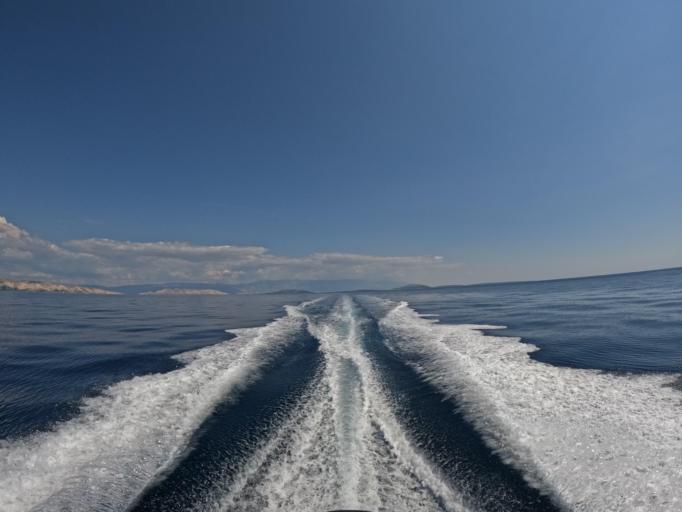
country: HR
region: Primorsko-Goranska
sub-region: Grad Krk
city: Krk
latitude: 44.9160
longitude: 14.5775
